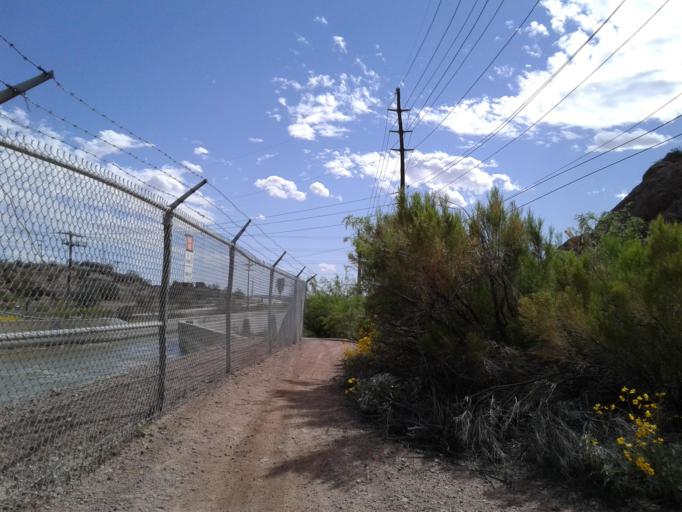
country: US
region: Arizona
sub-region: Maricopa County
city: Tempe Junction
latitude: 33.4486
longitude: -111.9406
